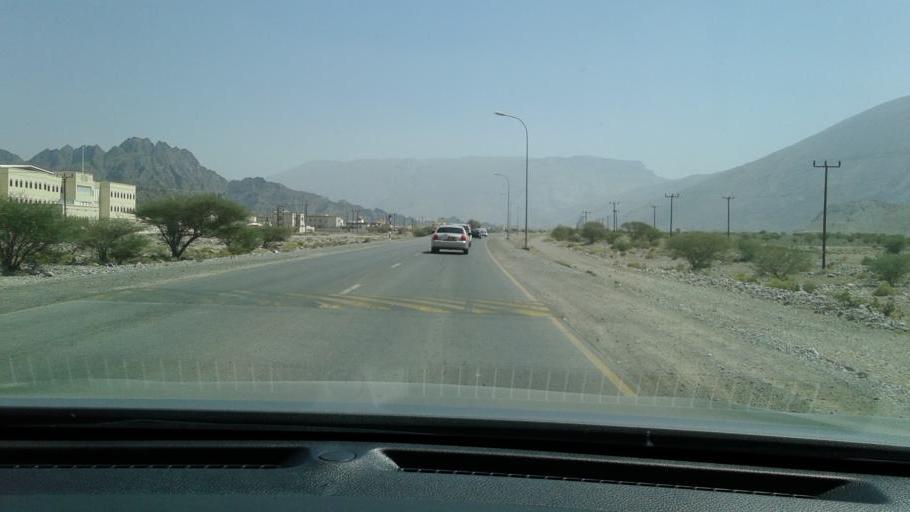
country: OM
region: Al Batinah
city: Rustaq
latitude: 23.3598
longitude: 57.4800
